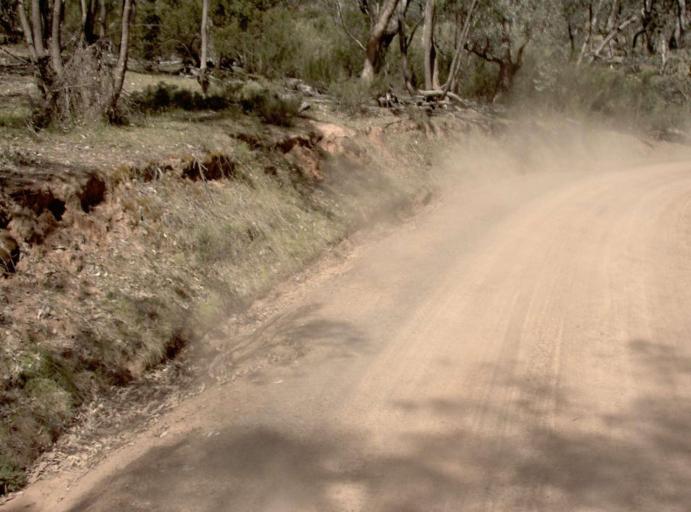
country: AU
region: New South Wales
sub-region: Snowy River
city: Jindabyne
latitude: -37.0521
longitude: 148.5383
